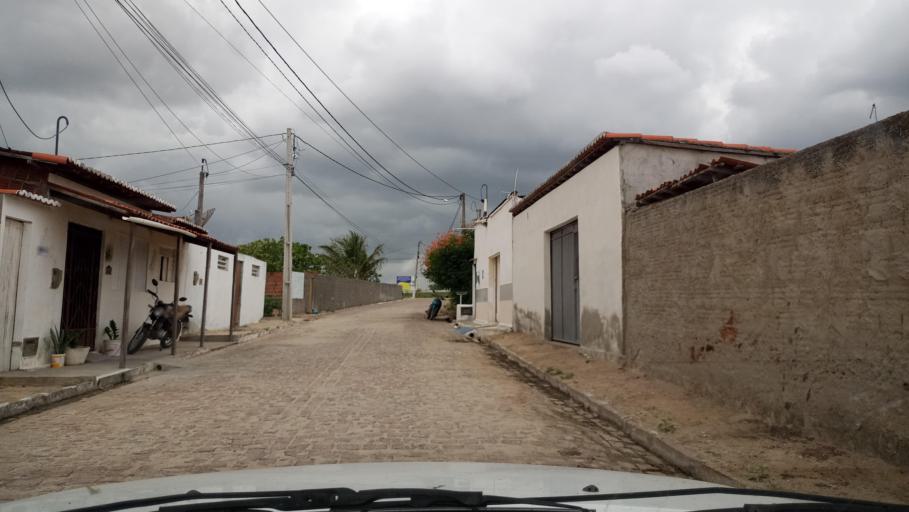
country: BR
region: Rio Grande do Norte
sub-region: Tangara
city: Tangara
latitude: -6.0993
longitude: -35.7124
